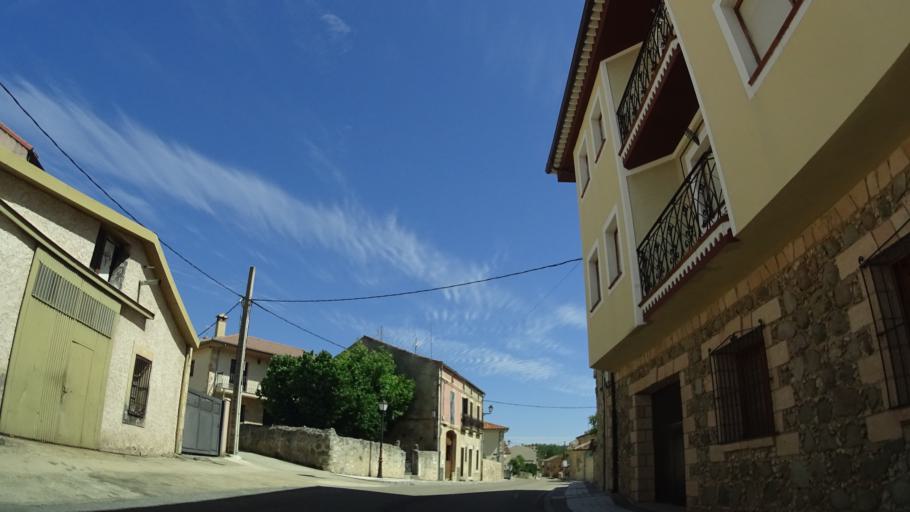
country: ES
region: Castille and Leon
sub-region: Provincia de Segovia
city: Pradena
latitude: 41.1371
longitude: -3.6881
